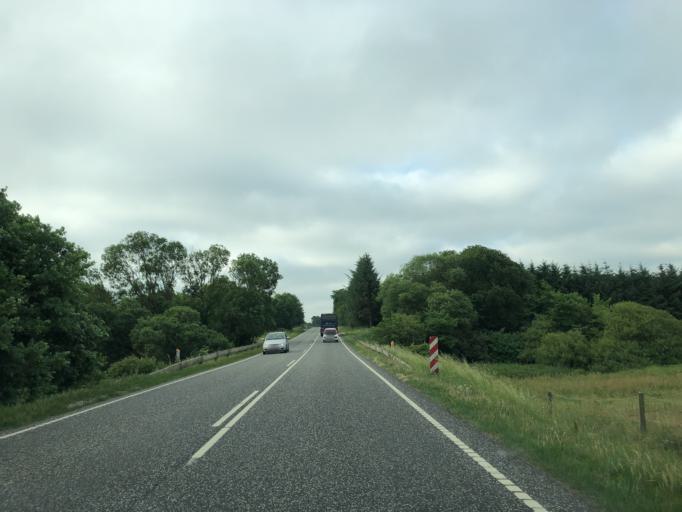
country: DK
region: South Denmark
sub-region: Vejle Kommune
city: Give
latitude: 55.7820
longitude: 9.2773
